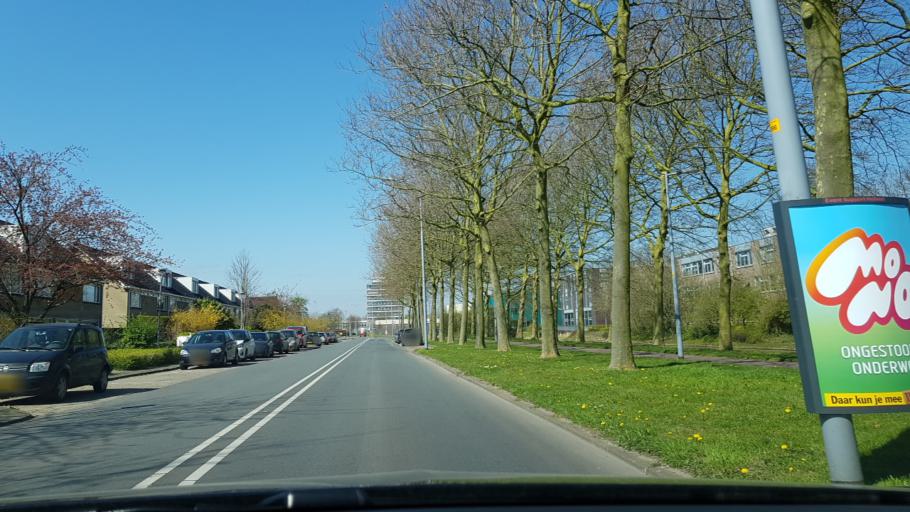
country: NL
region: South Holland
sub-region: Gemeente Hillegom
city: Hillegom
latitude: 52.2708
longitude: 4.6341
